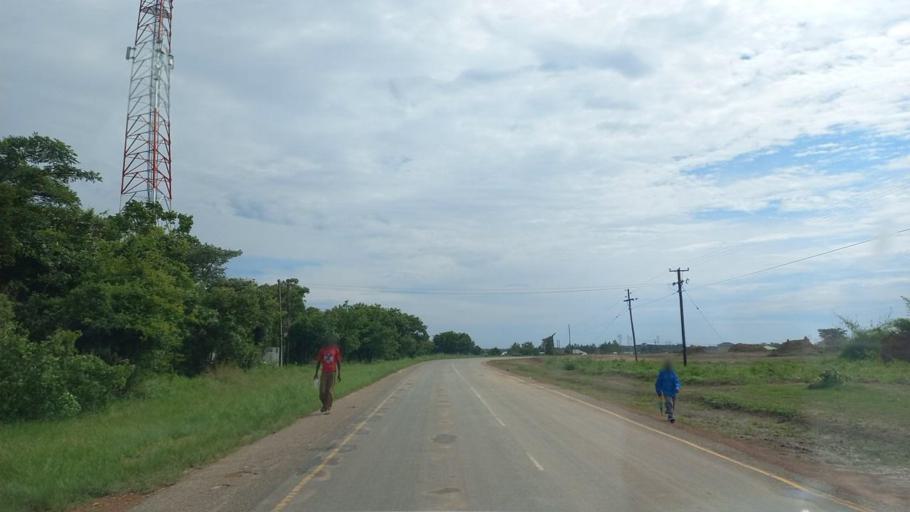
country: ZM
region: Copperbelt
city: Kitwe
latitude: -12.8741
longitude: 28.3309
